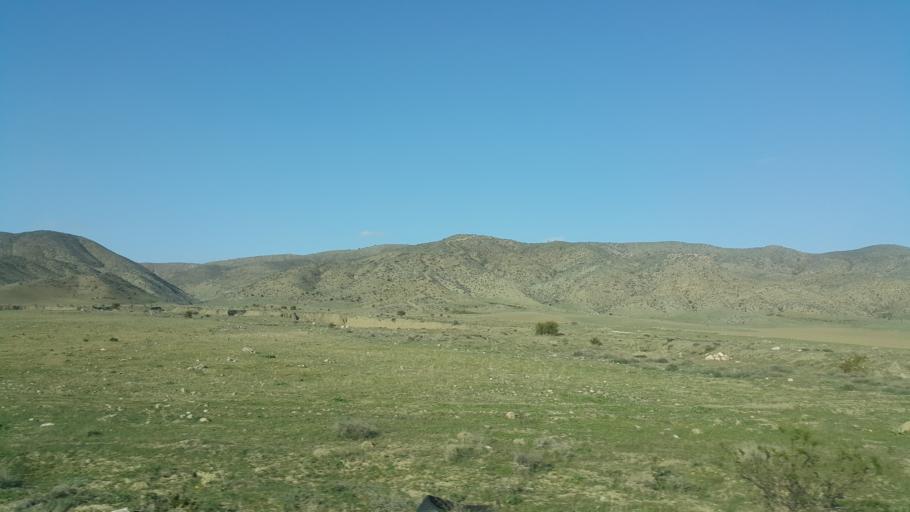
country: TR
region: Ankara
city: Sereflikochisar
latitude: 38.7996
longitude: 33.6199
